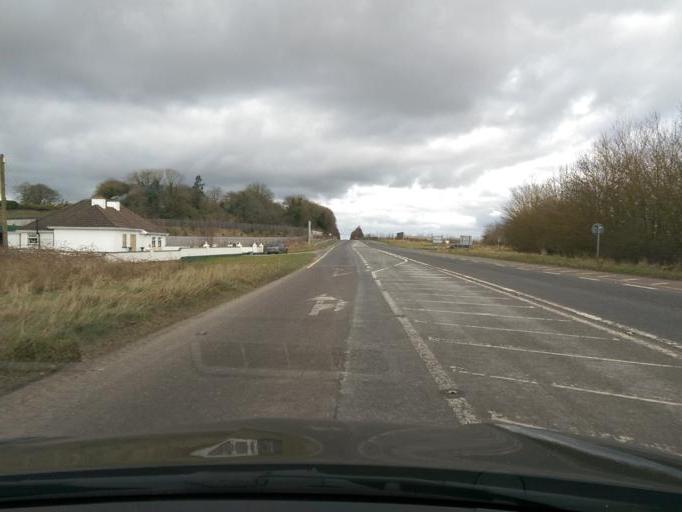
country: IE
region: Leinster
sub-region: An Iarmhi
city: Moate
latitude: 53.3899
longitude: -7.7726
